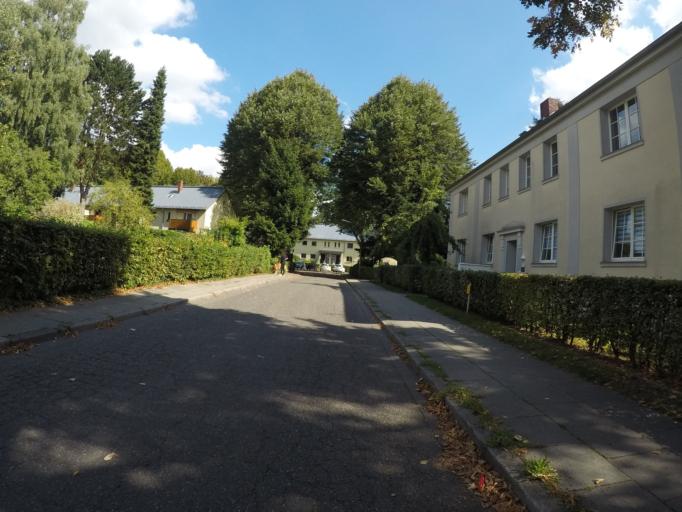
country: DE
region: Hamburg
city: Eidelstedt
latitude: 53.6065
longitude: 9.8959
